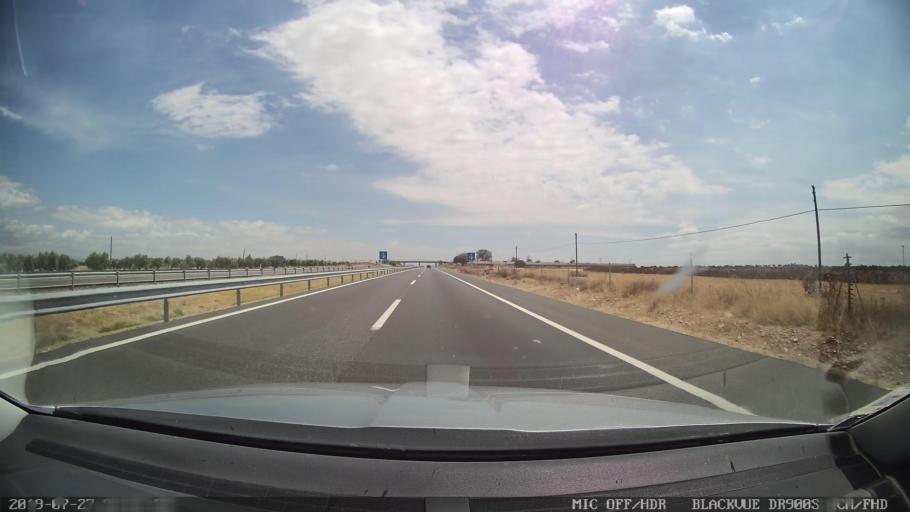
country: ES
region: Castille-La Mancha
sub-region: Province of Toledo
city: Lucillos
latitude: 40.0167
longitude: -4.5792
